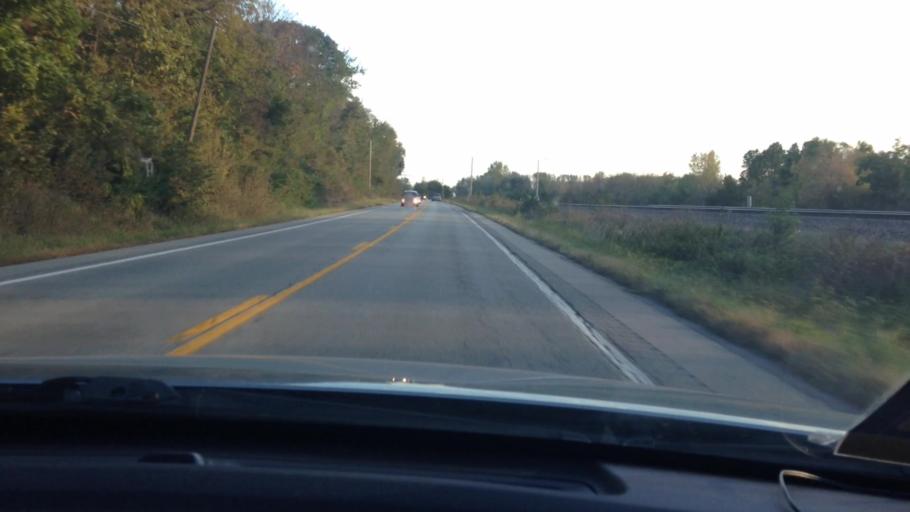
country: US
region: Kansas
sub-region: Leavenworth County
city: Leavenworth
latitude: 39.3174
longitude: -94.8532
